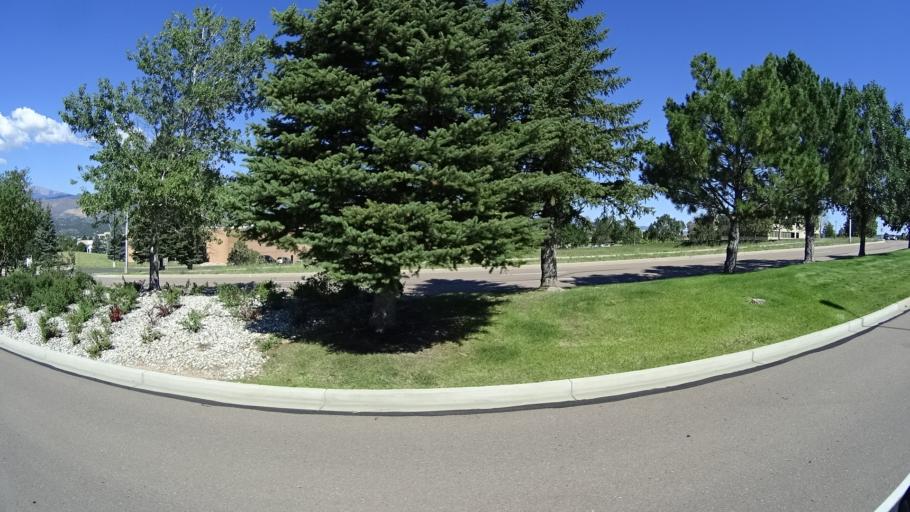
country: US
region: Colorado
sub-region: El Paso County
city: Air Force Academy
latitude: 38.9582
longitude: -104.7851
